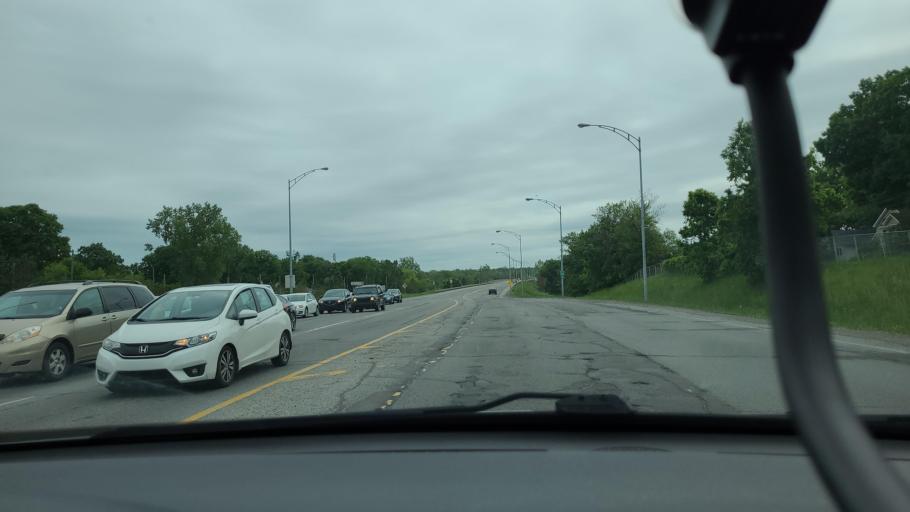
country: CA
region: Quebec
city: Bois-des-Filion
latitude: 45.6650
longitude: -73.7589
